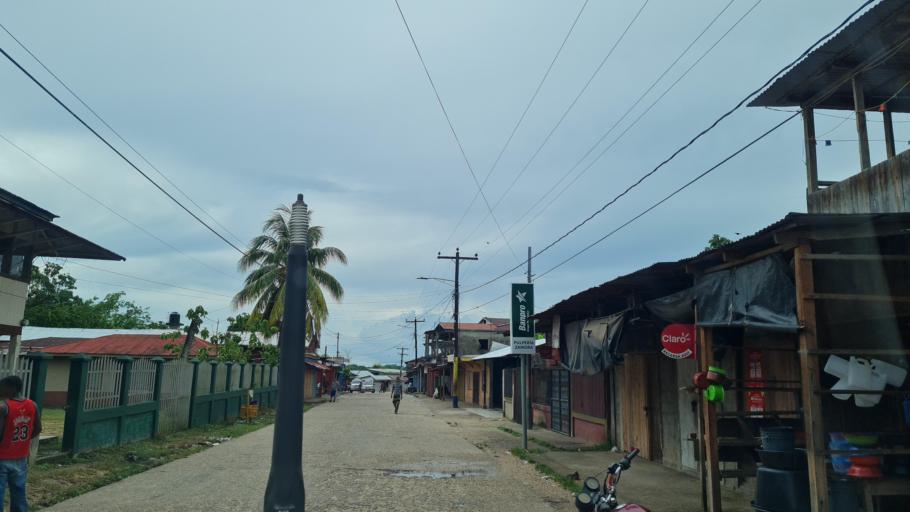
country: NI
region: Atlantico Norte (RAAN)
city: Waspam
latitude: 14.7437
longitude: -83.9718
